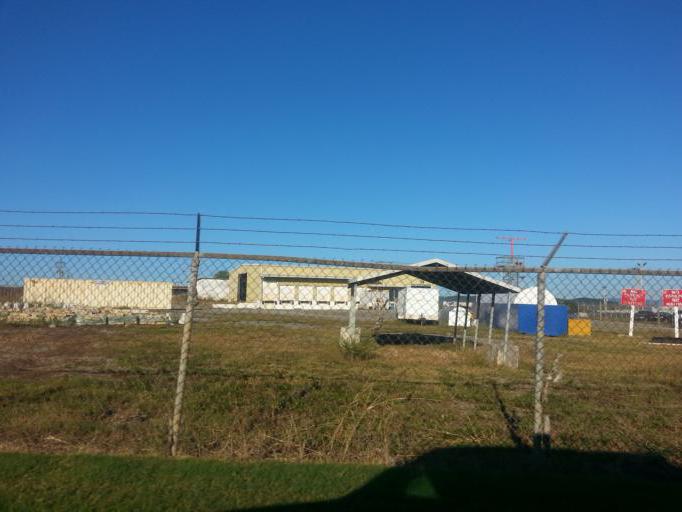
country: US
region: Tennessee
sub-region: Blount County
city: Alcoa
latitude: 35.8259
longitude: -83.9798
